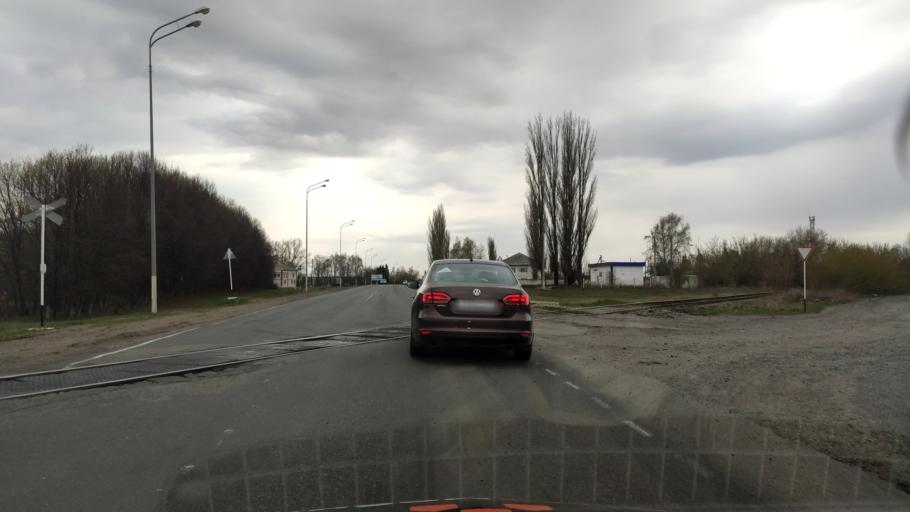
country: RU
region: Kursk
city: Gorshechnoye
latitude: 51.5275
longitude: 38.0228
